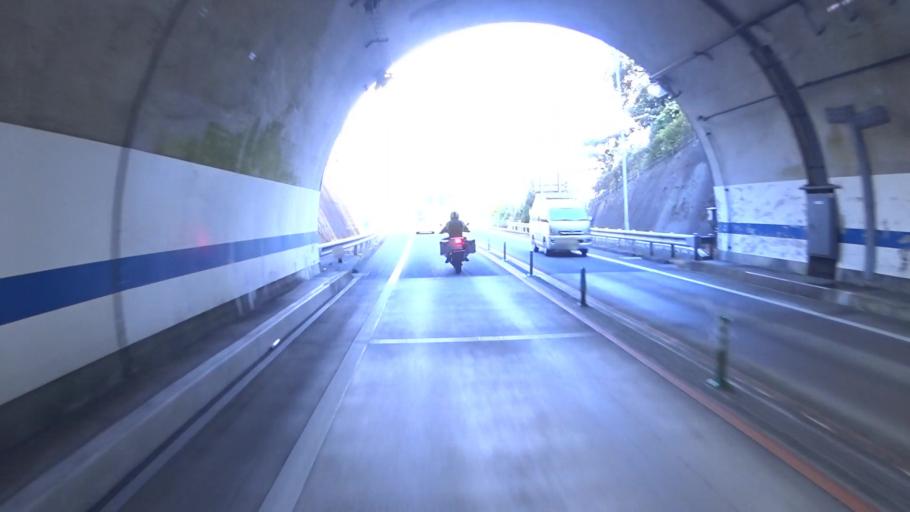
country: JP
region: Kyoto
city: Maizuru
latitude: 35.4151
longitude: 135.2197
